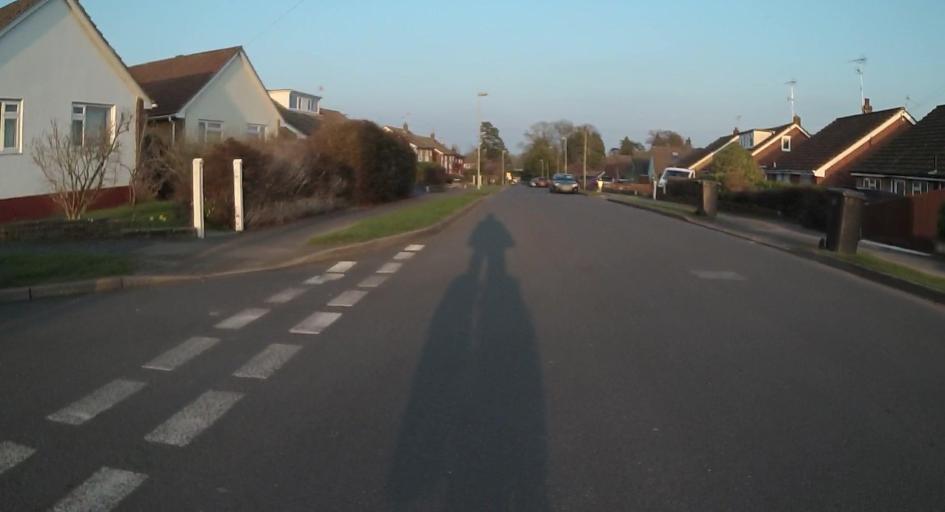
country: GB
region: England
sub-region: Hampshire
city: Alton
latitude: 51.1536
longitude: -0.9793
